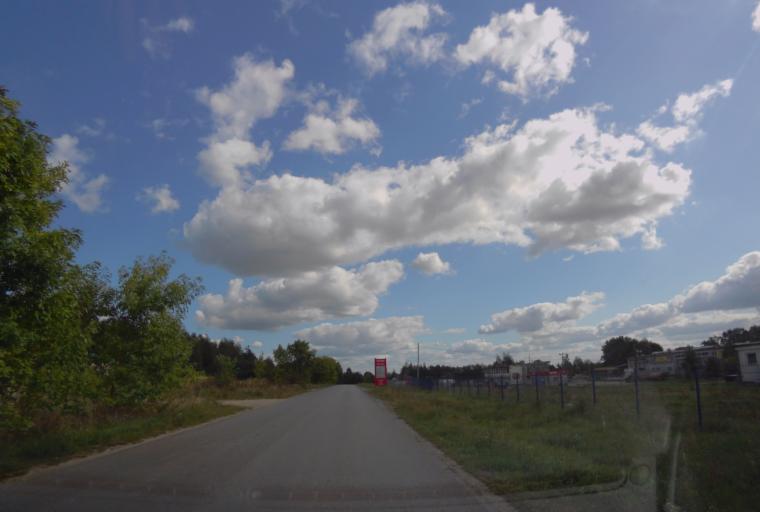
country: PL
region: Subcarpathian Voivodeship
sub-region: Tarnobrzeg
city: Tarnobrzeg
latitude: 50.5156
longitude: 21.6421
